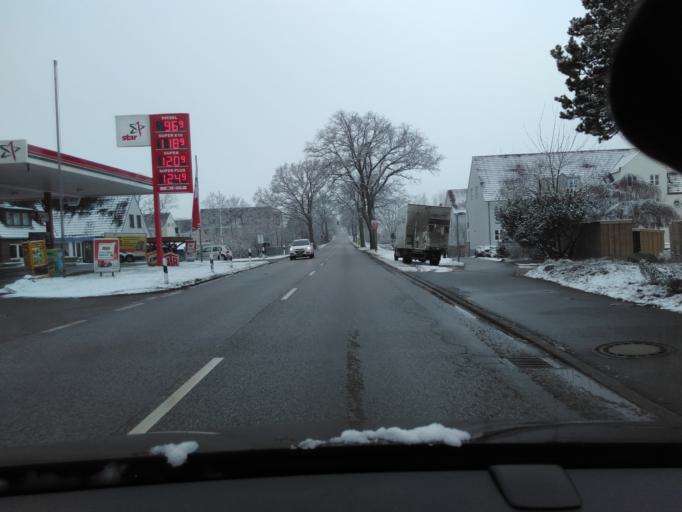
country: DE
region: Schleswig-Holstein
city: Ahrensbok
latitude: 54.0143
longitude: 10.5677
